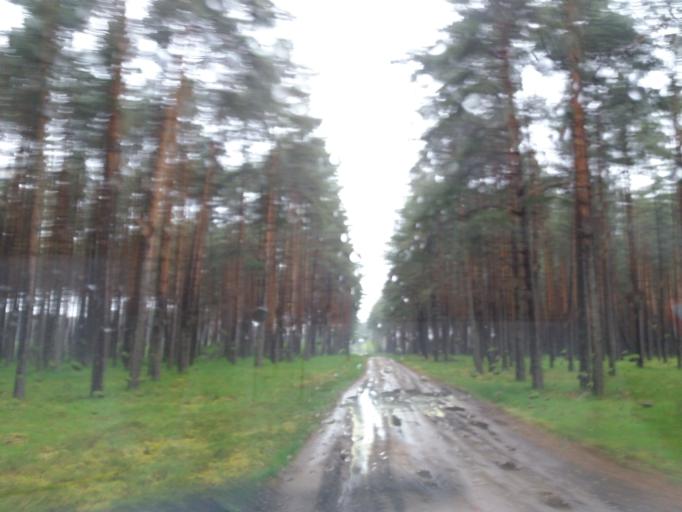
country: PL
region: West Pomeranian Voivodeship
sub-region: Powiat drawski
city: Kalisz Pomorski
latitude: 53.1662
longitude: 15.9805
